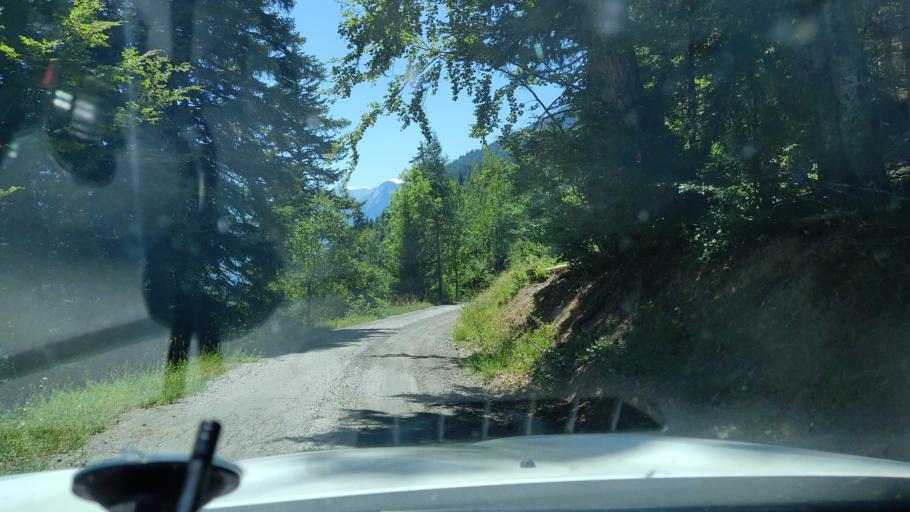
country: FR
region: Rhone-Alpes
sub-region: Departement de la Savoie
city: Salins-les-Thermes
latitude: 45.4730
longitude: 6.5088
